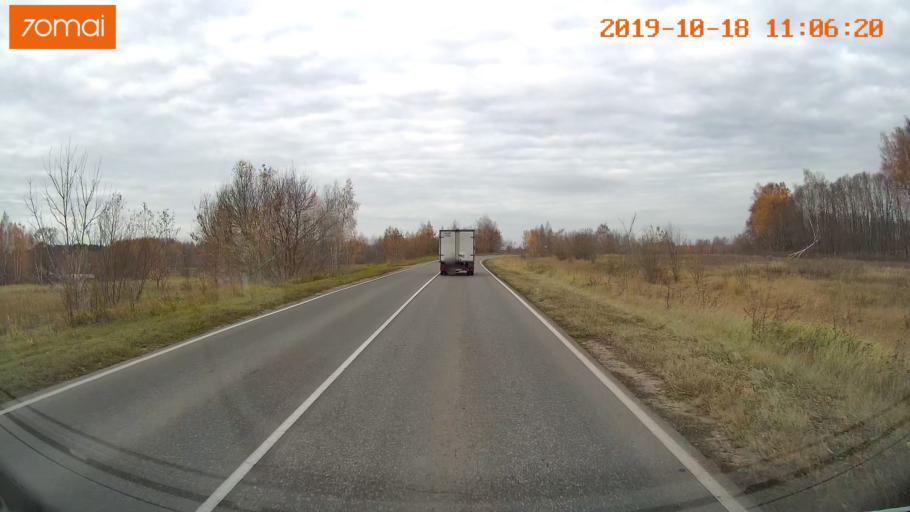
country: RU
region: Tula
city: Kimovsk
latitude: 53.9177
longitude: 38.5382
